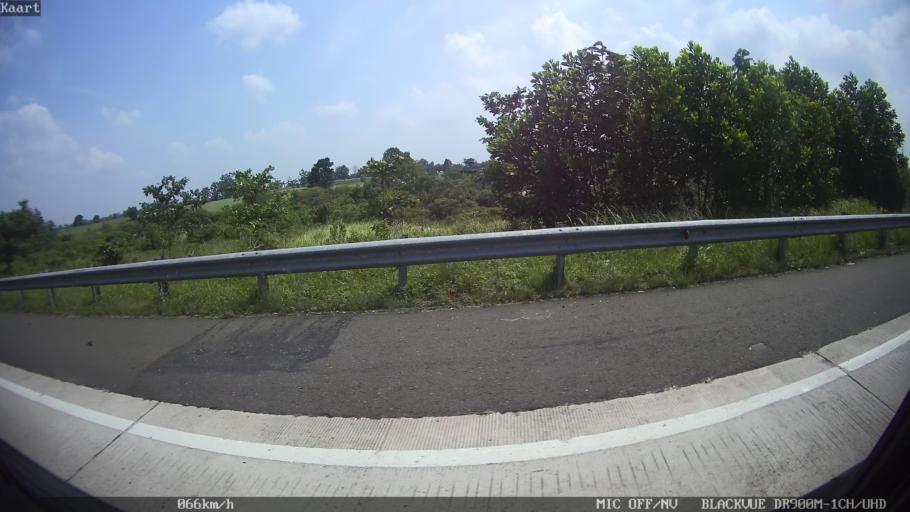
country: ID
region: Lampung
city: Kedaton
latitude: -5.3420
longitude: 105.3133
